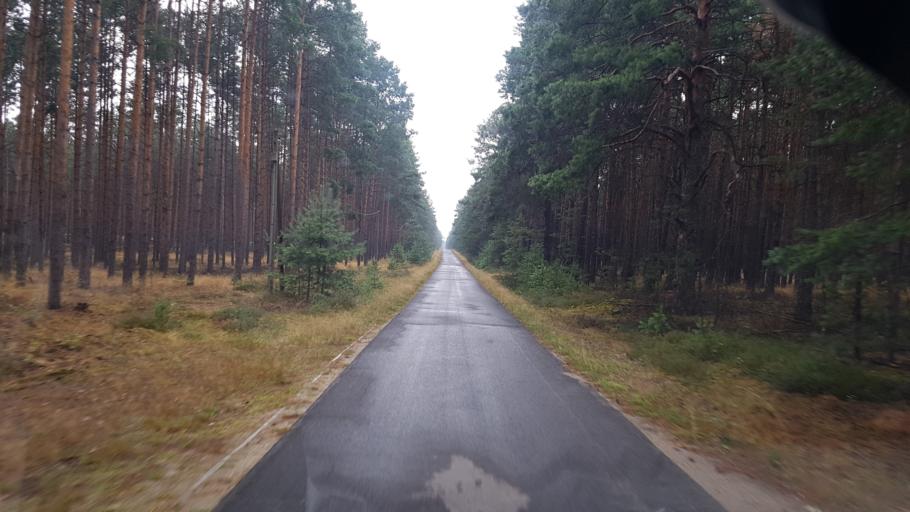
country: DE
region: Brandenburg
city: Finsterwalde
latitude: 51.6466
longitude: 13.7848
